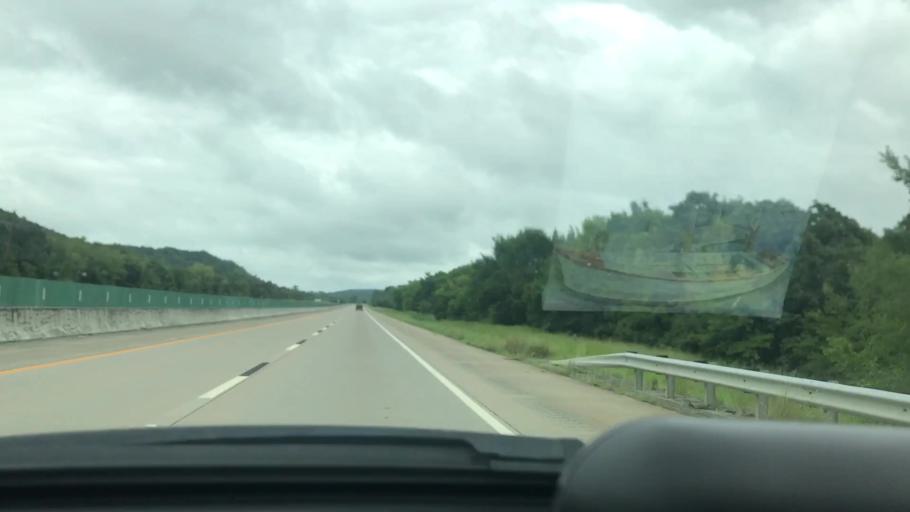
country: US
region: Oklahoma
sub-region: Pittsburg County
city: Krebs
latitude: 35.0844
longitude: -95.7017
